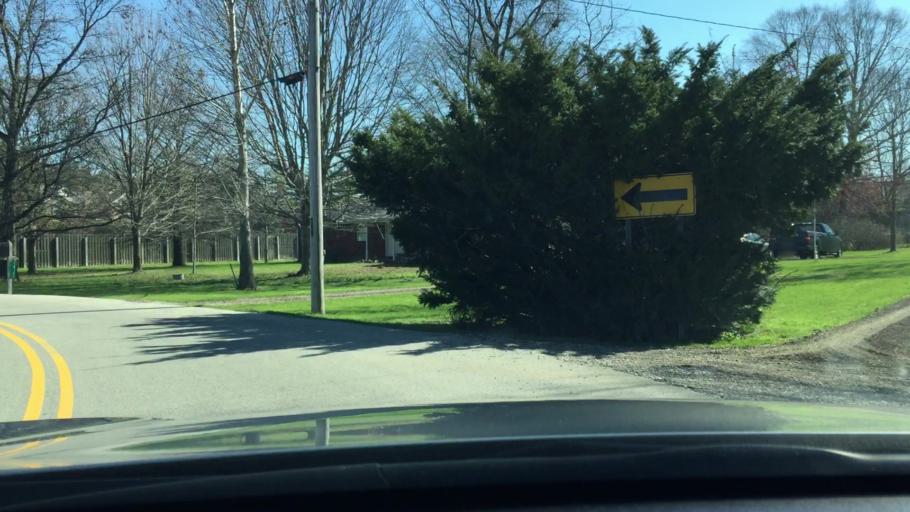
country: US
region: Indiana
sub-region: Hamilton County
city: Carmel
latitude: 39.9942
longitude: -86.0612
